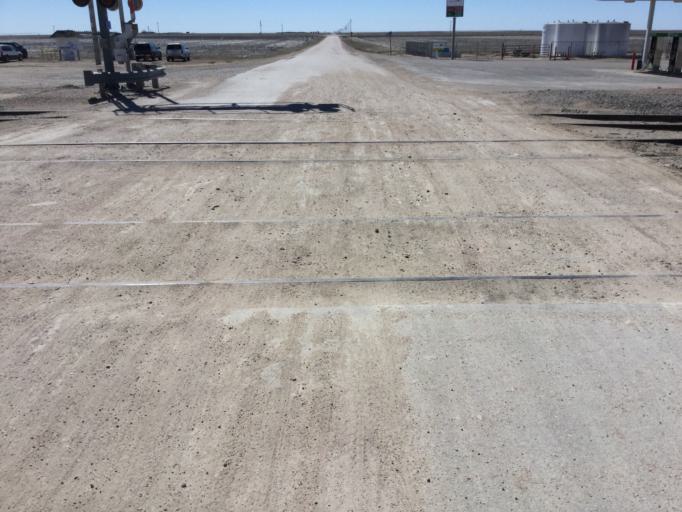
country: US
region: Kansas
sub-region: Wichita County
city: Leoti
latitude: 38.4863
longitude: -101.2201
